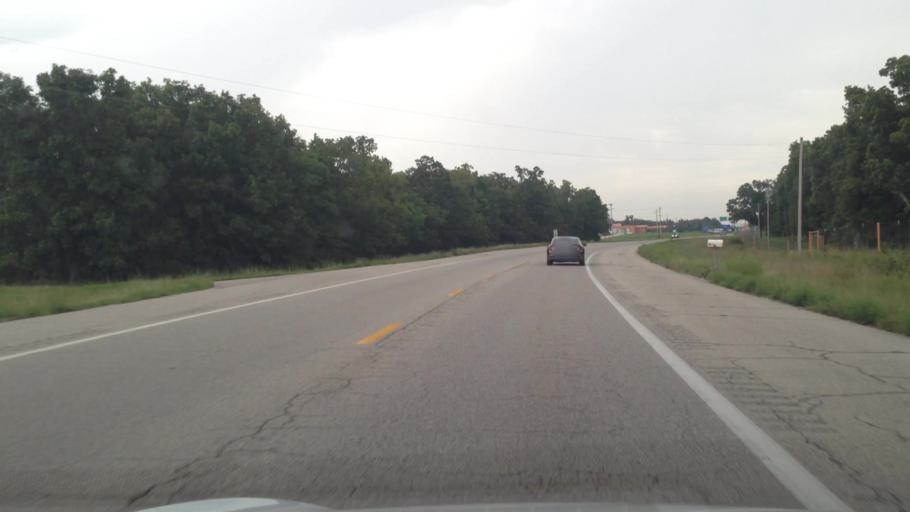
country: US
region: Kansas
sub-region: Cherokee County
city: Galena
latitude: 37.0069
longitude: -94.6201
